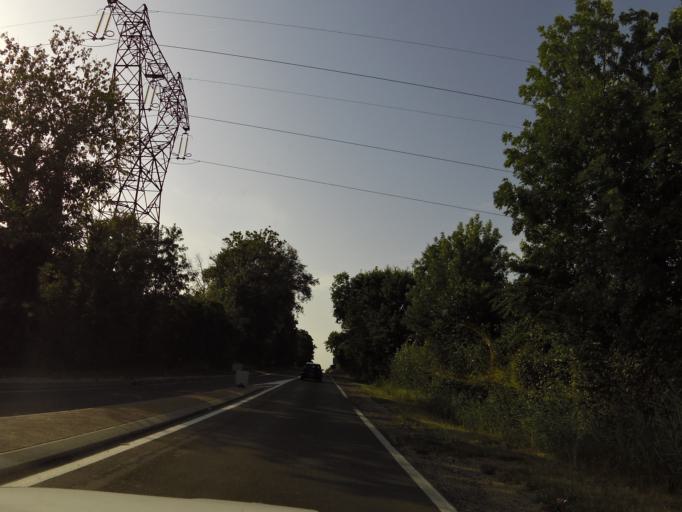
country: FR
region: Rhone-Alpes
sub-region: Departement de l'Ain
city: Meximieux
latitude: 45.9155
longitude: 5.1922
